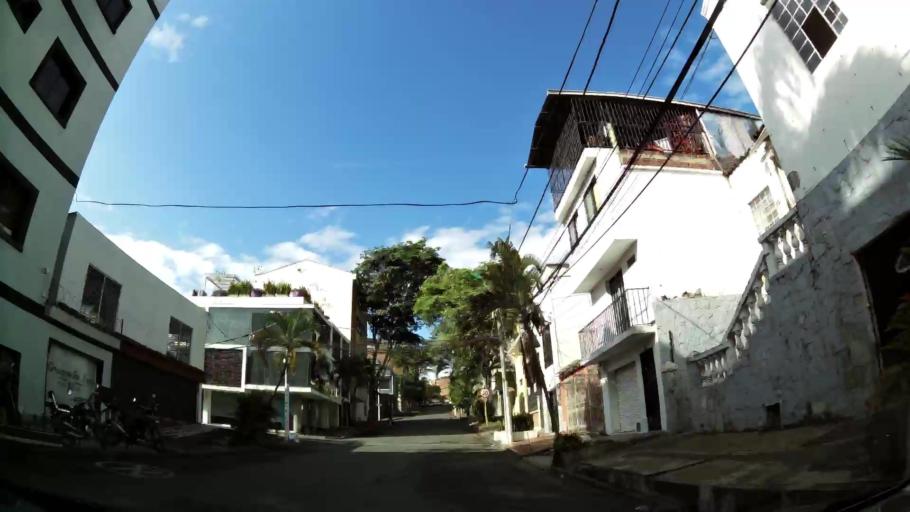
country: CO
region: Valle del Cauca
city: Cali
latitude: 3.4597
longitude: -76.5351
